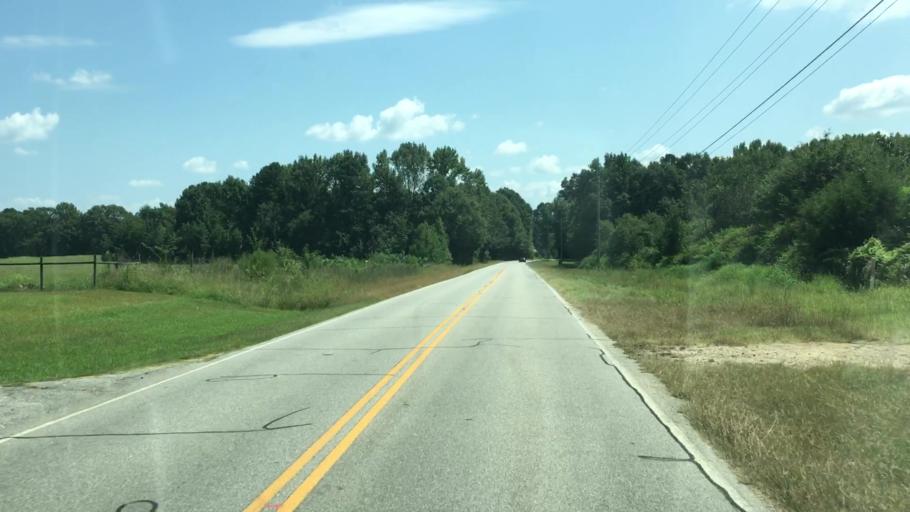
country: US
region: Georgia
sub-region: Oconee County
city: Watkinsville
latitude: 33.8507
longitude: -83.4504
